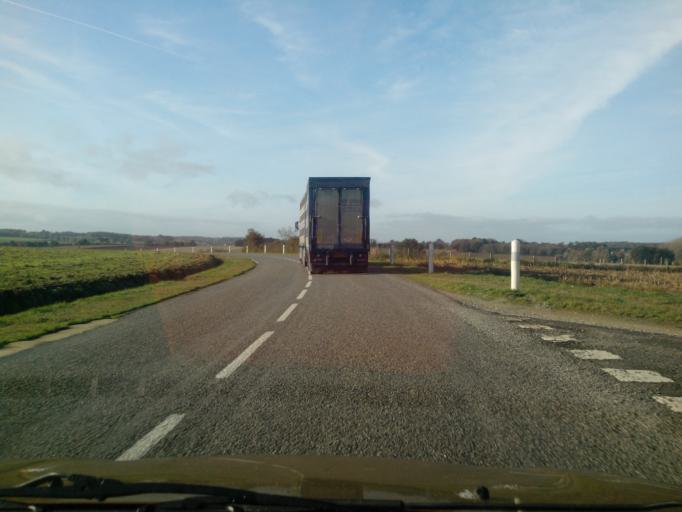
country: FR
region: Brittany
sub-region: Departement du Morbihan
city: Josselin
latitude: 48.0037
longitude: -2.5050
